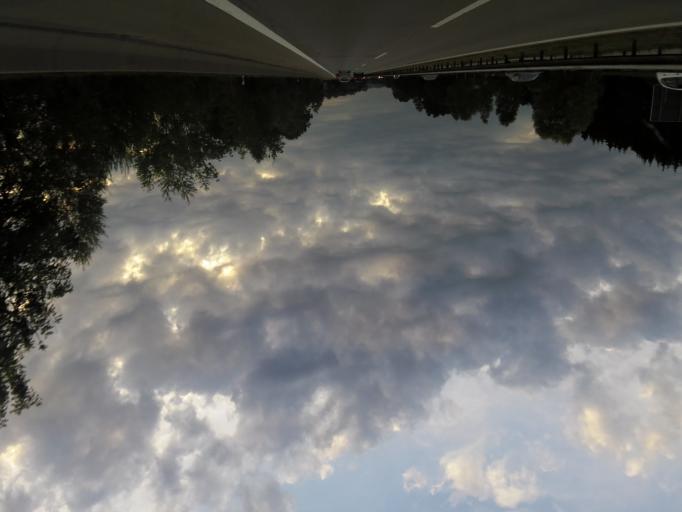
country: DE
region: Bavaria
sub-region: Upper Bavaria
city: Chiemsee
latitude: 47.8340
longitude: 12.4225
